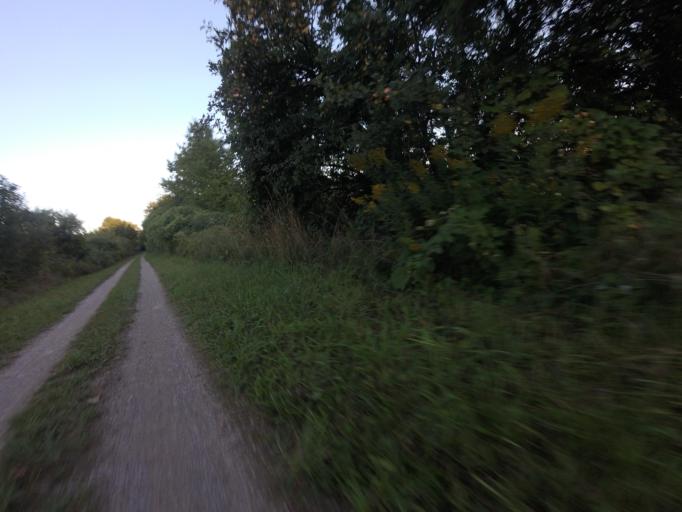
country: CA
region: Ontario
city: Goderich
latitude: 43.7488
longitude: -81.6504
